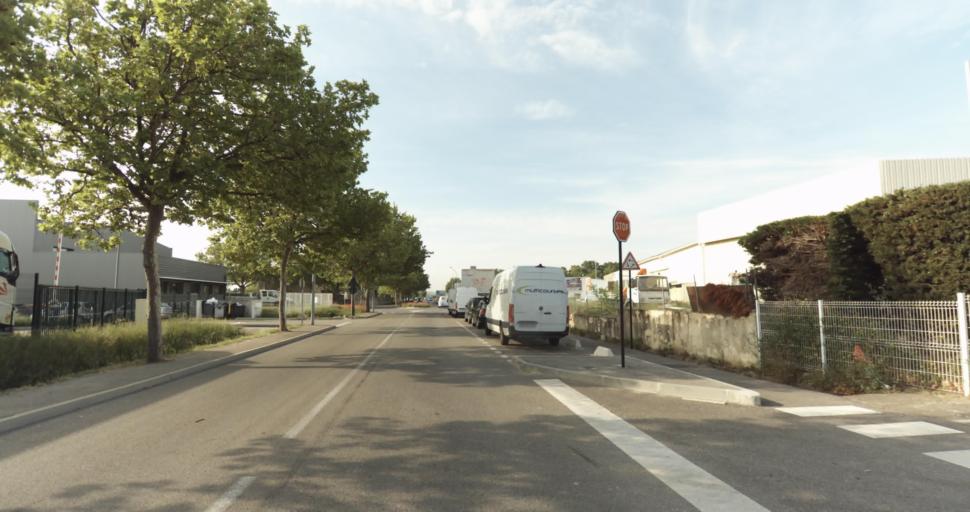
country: FR
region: Languedoc-Roussillon
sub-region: Departement du Gard
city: Rodilhan
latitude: 43.8366
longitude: 4.4169
